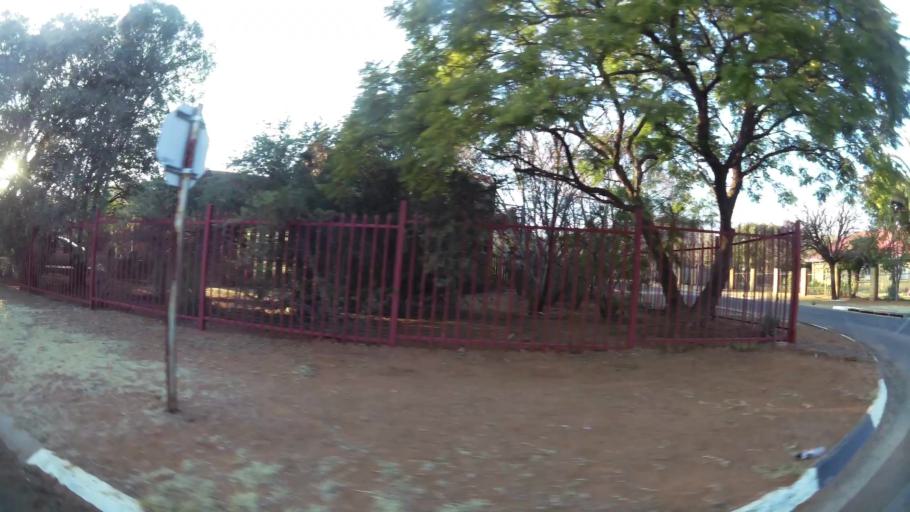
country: ZA
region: Orange Free State
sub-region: Mangaung Metropolitan Municipality
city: Bloemfontein
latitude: -29.0906
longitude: 26.1541
